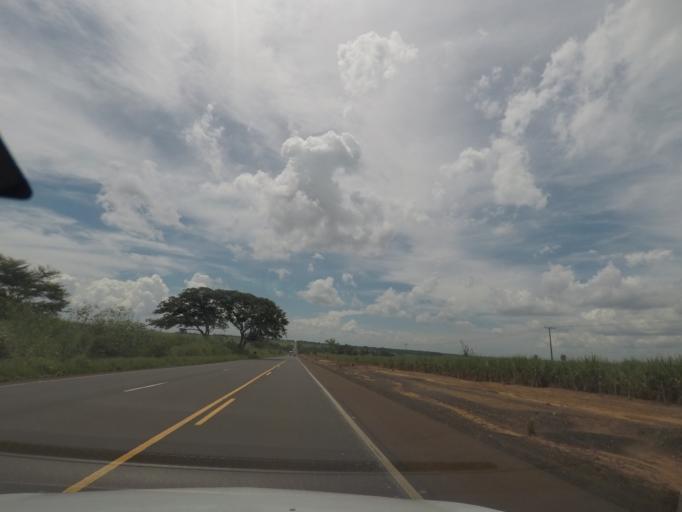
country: BR
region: Sao Paulo
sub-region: Barretos
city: Barretos
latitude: -20.3776
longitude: -48.6435
